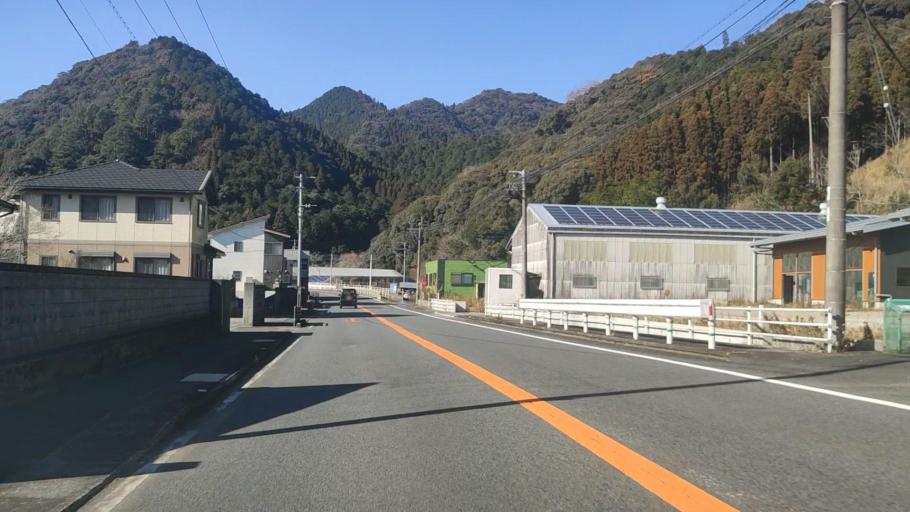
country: JP
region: Oita
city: Saiki
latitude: 32.9852
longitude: 131.8477
